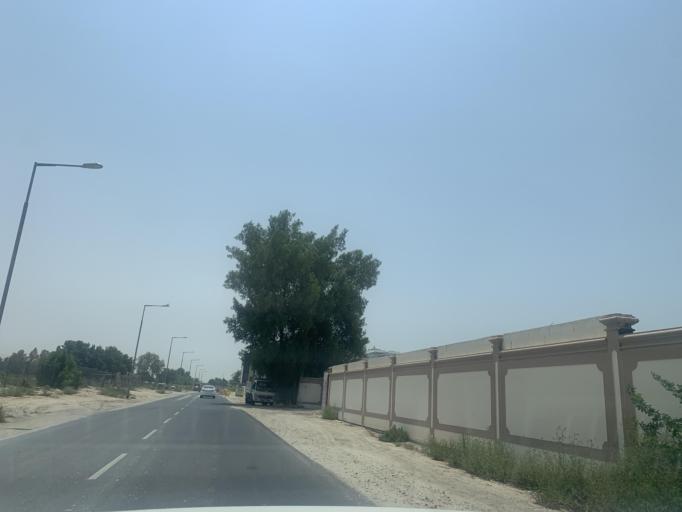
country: BH
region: Central Governorate
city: Madinat Hamad
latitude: 26.1480
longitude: 50.4661
